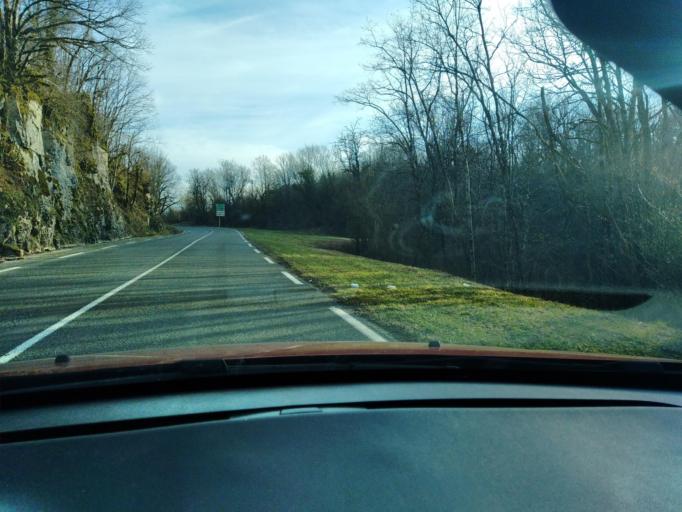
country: FR
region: Franche-Comte
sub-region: Departement du Jura
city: Perrigny
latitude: 46.6202
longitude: 5.6111
